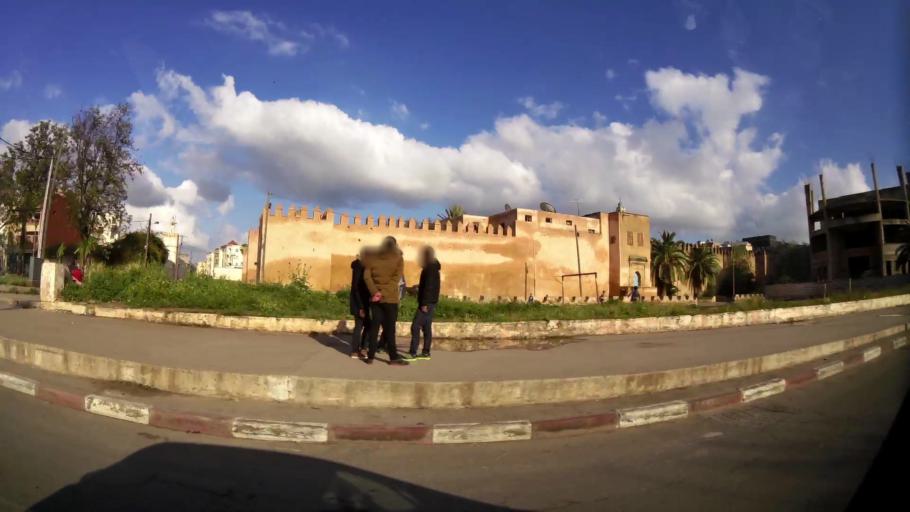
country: MA
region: Chaouia-Ouardigha
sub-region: Settat Province
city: Settat
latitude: 33.0038
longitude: -7.6217
